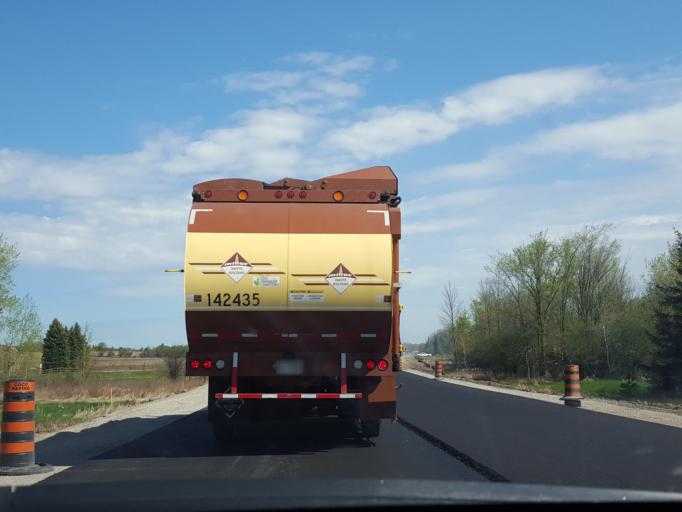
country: CA
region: Ontario
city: Uxbridge
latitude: 44.0721
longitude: -78.9354
